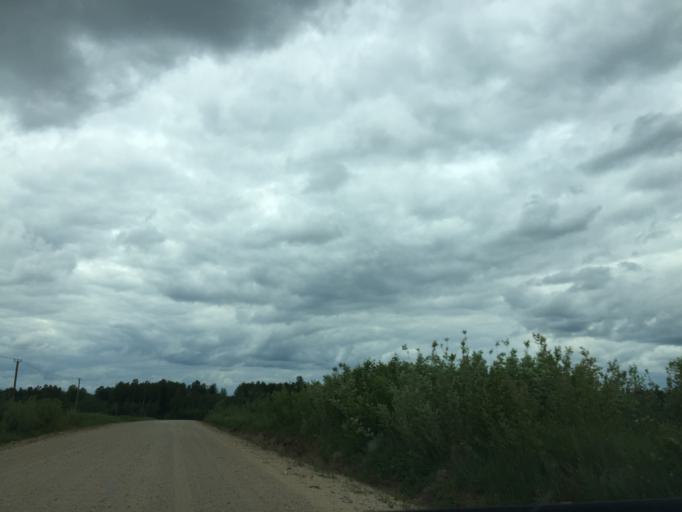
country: LV
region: Dagda
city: Dagda
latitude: 55.9856
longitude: 27.6065
